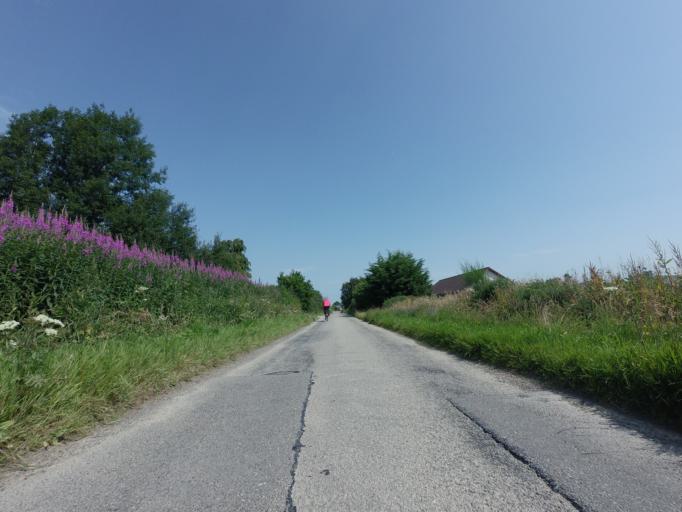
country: GB
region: Scotland
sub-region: Highland
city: Tain
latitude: 57.8006
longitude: -4.0676
